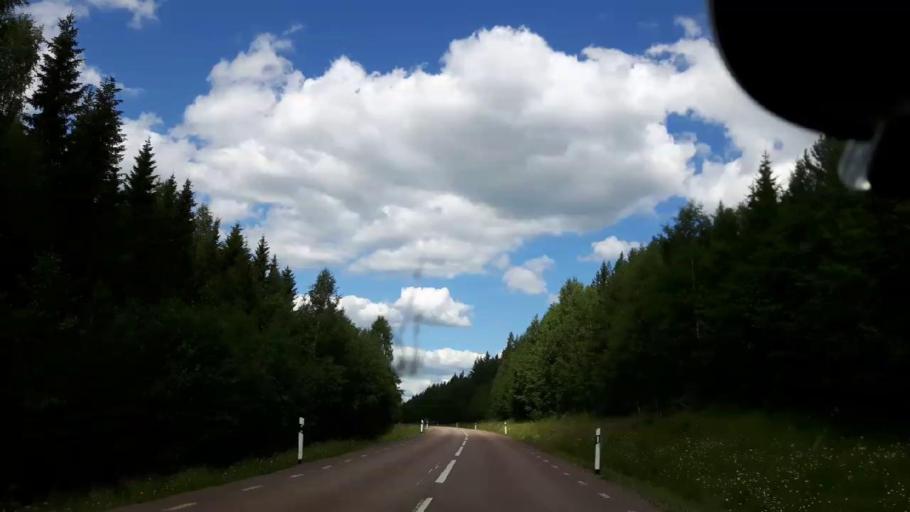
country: SE
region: Jaemtland
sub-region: Ragunda Kommun
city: Hammarstrand
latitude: 62.9212
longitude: 16.7036
